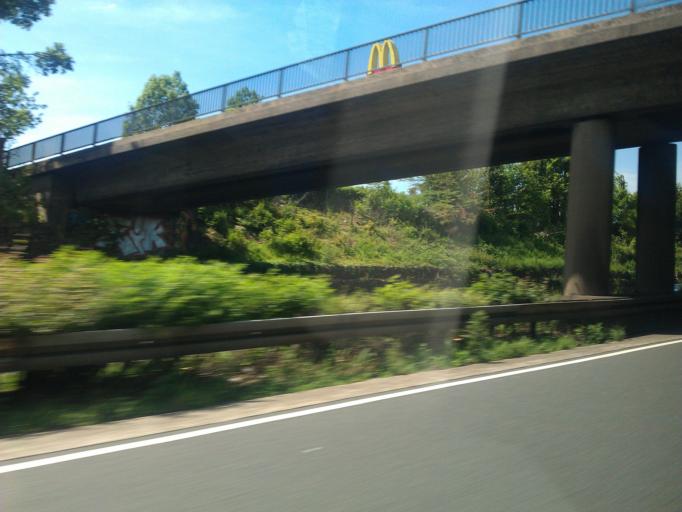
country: DE
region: North Rhine-Westphalia
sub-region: Regierungsbezirk Koln
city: Bad Honnef
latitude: 50.6840
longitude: 7.2770
